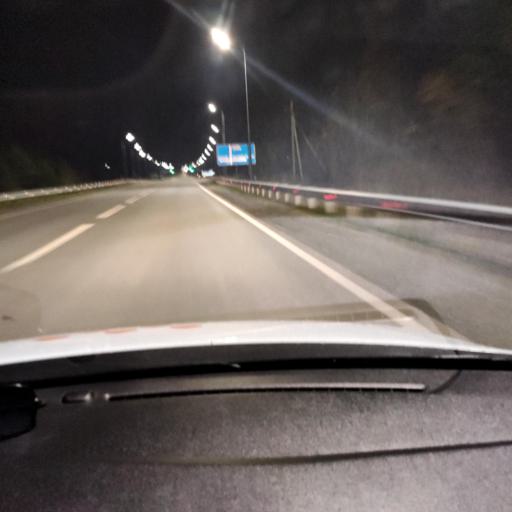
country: RU
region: Tatarstan
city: Stolbishchi
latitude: 55.6381
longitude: 49.1113
